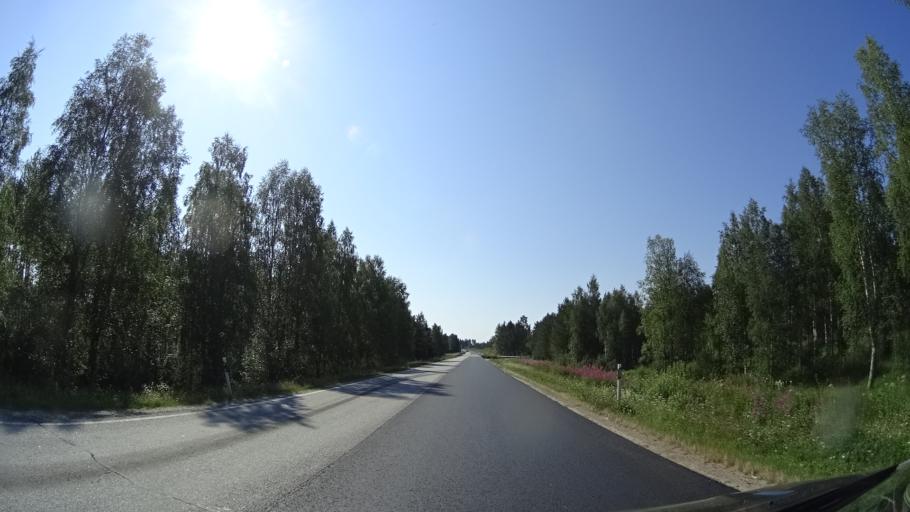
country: FI
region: North Karelia
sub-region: Joensuu
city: Juuka
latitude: 63.2361
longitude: 29.2833
